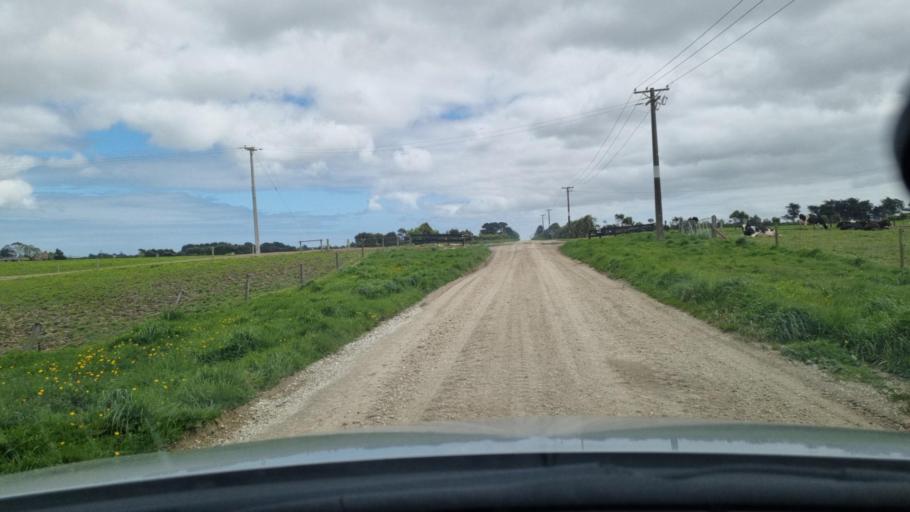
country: NZ
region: Southland
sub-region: Invercargill City
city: Invercargill
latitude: -46.4432
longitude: 168.4151
